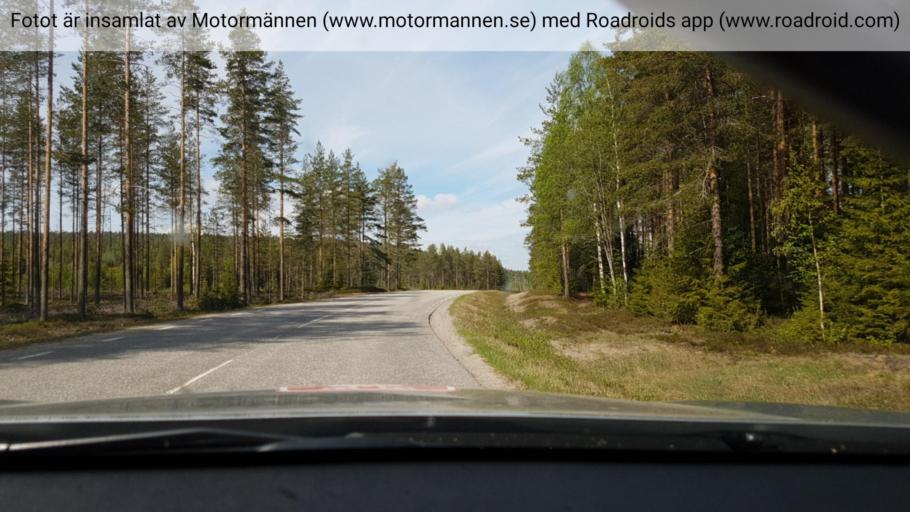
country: SE
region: Vaesterbotten
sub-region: Umea Kommun
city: Roback
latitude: 63.8403
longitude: 20.0946
